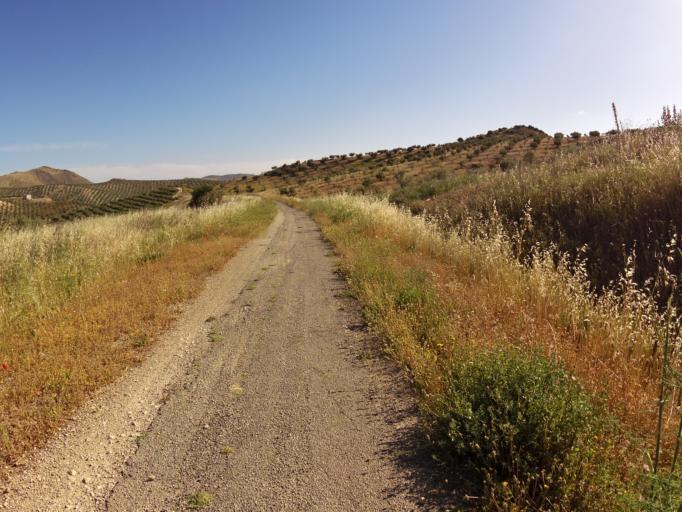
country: ES
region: Andalusia
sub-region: Province of Cordoba
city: Fuente-Tojar
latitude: 37.5810
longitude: -4.1773
